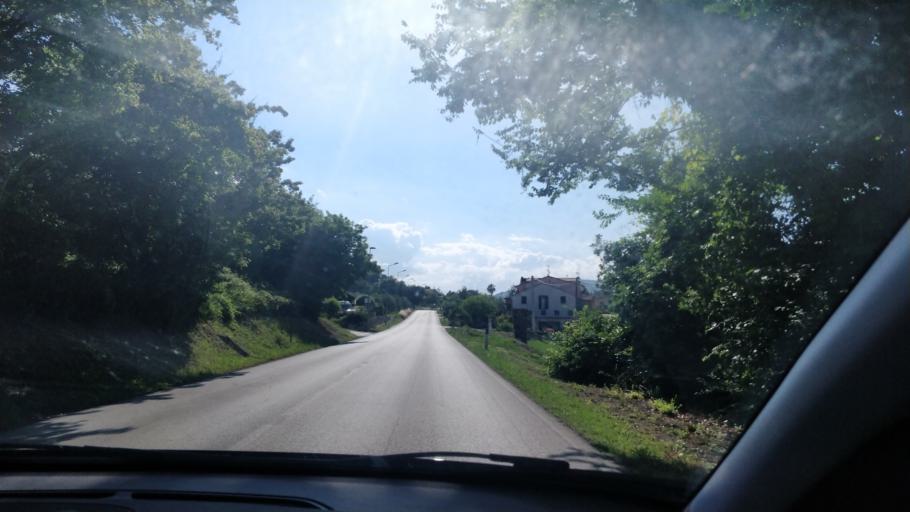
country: IT
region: The Marches
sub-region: Provincia di Ascoli Piceno
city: Cupra Marittima
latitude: 43.0357
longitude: 13.8409
